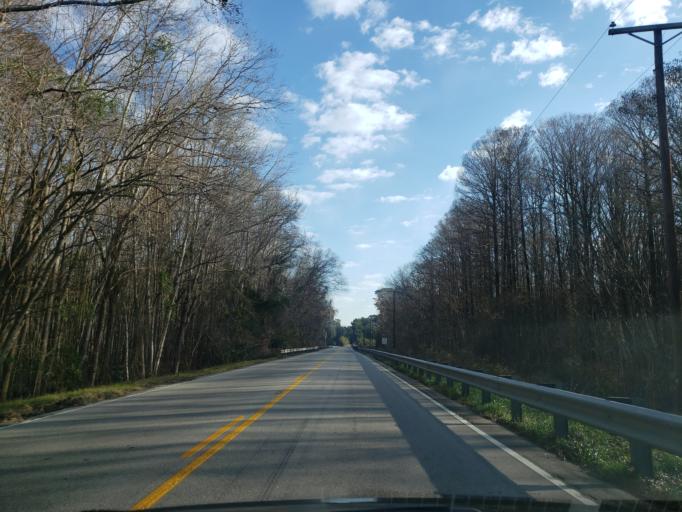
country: US
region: Georgia
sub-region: Chatham County
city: Port Wentworth
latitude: 32.1782
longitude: -81.0837
